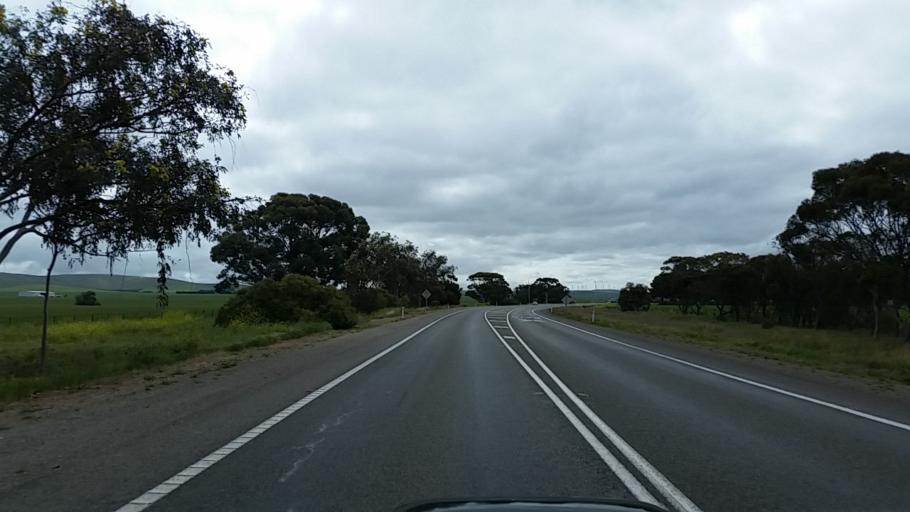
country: AU
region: South Australia
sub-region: Clare and Gilbert Valleys
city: Clare
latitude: -33.7906
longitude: 138.2079
